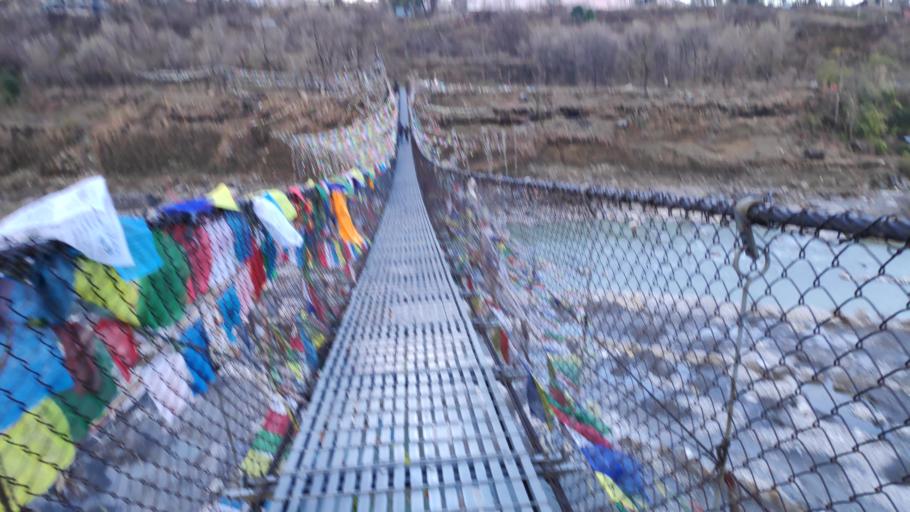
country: NP
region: Western Region
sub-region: Gandaki Zone
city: Pokhara
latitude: 28.2573
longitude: 83.9647
